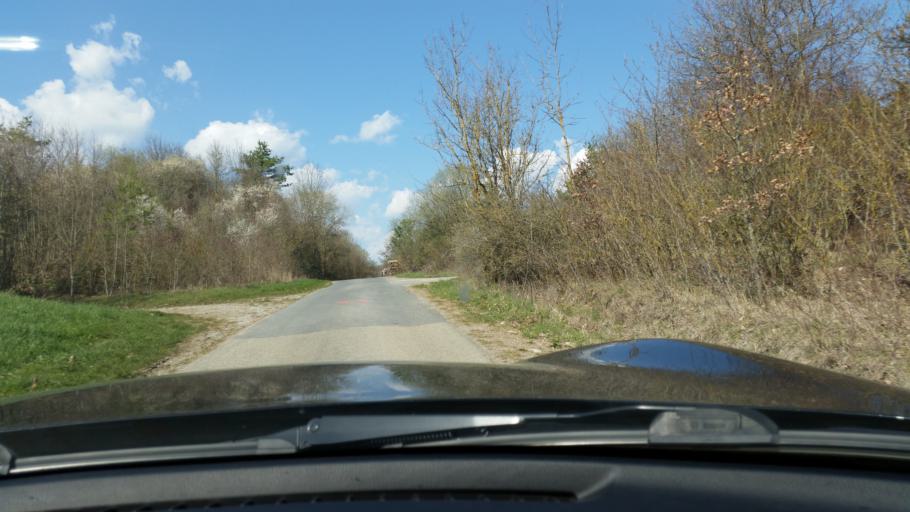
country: DE
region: Baden-Wuerttemberg
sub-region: Regierungsbezirk Stuttgart
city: Krautheim
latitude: 49.3797
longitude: 9.6048
